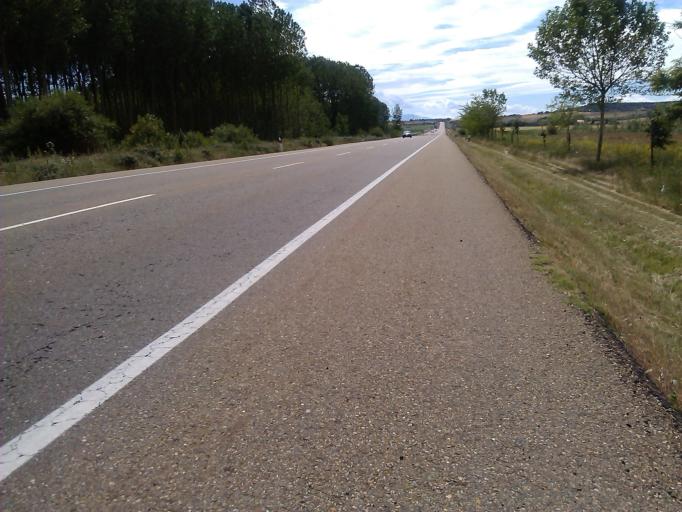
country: ES
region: Castille and Leon
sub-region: Provincia de Leon
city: Villarejo de Orbigo
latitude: 42.4541
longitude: -5.9086
